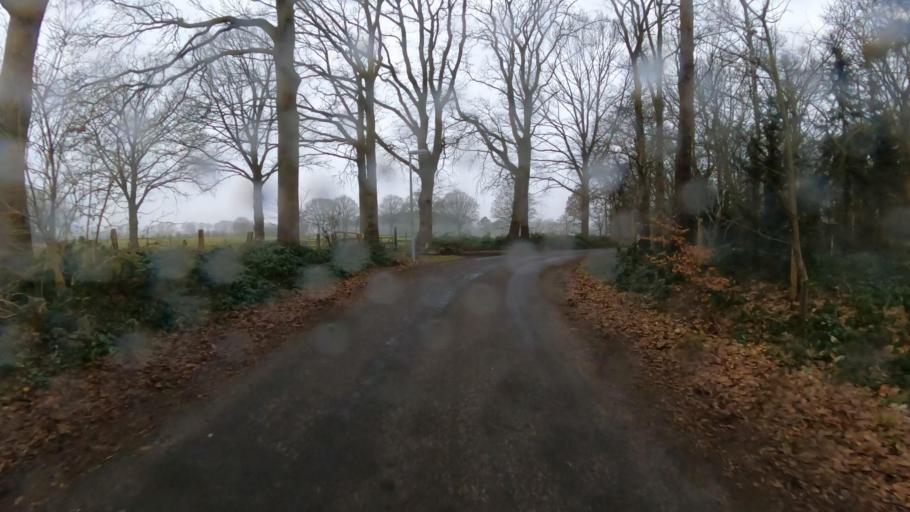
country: DE
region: Schleswig-Holstein
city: Appen
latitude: 53.6333
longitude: 9.7611
